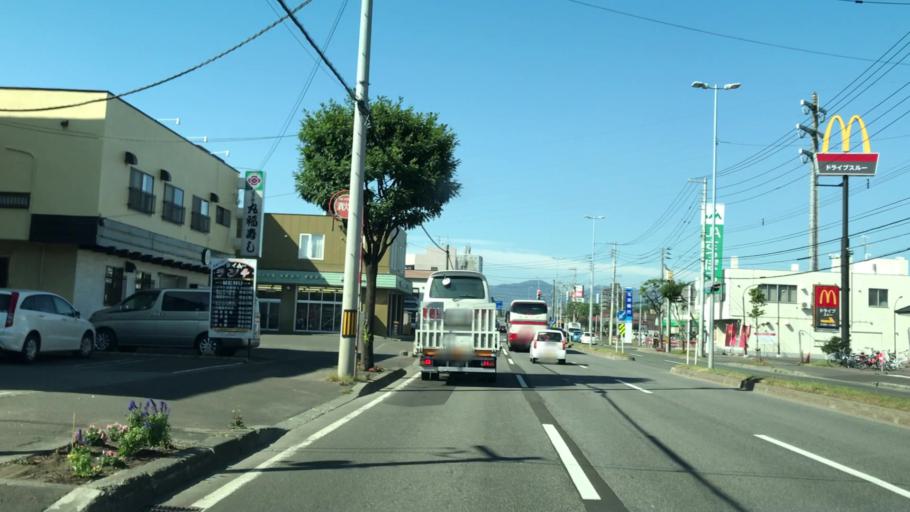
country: JP
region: Hokkaido
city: Sapporo
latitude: 43.0734
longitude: 141.4103
